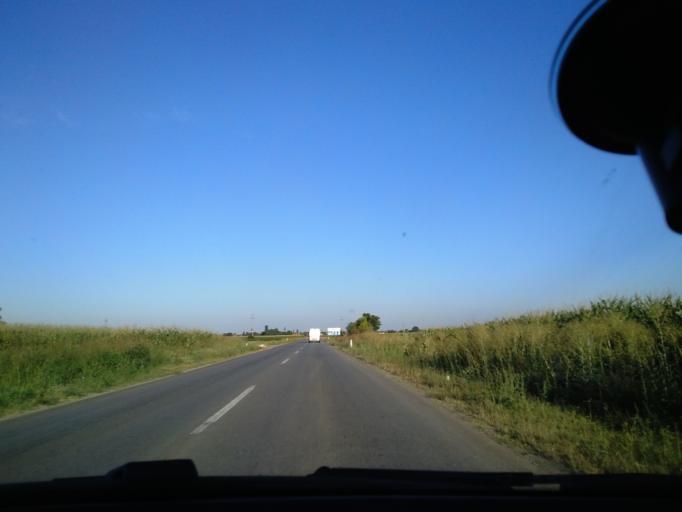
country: RS
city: Maglic
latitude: 45.4021
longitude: 19.4377
